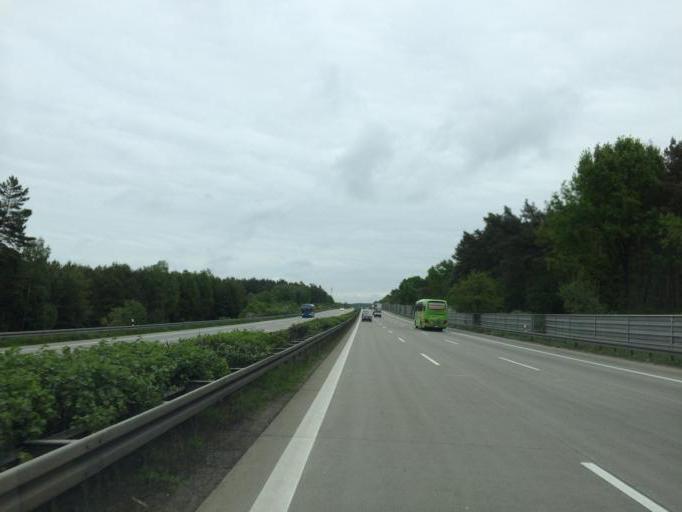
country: DE
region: Saxony-Anhalt
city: Moser
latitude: 52.2283
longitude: 11.7837
